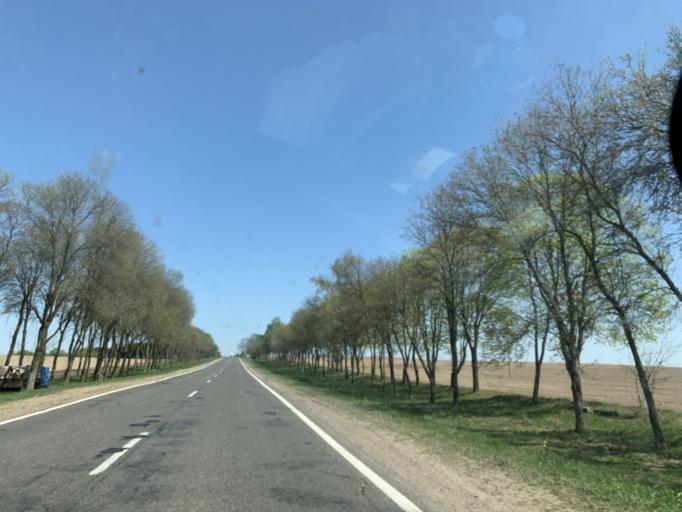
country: BY
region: Minsk
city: Nyasvizh
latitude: 53.2304
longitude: 26.7856
